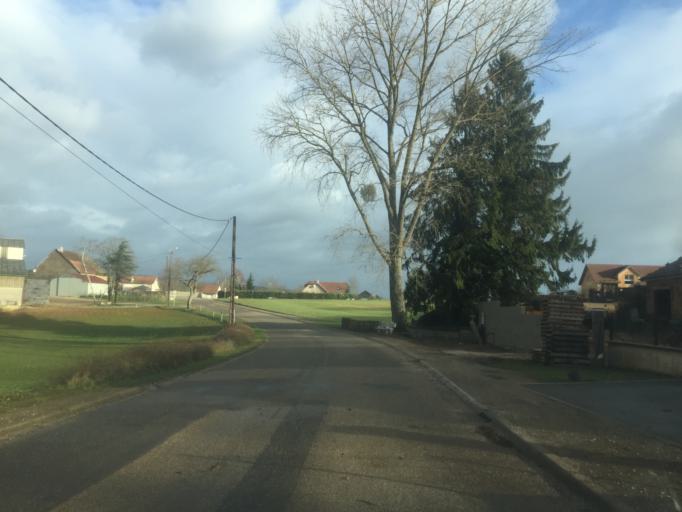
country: FR
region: Franche-Comte
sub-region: Departement du Jura
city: Orchamps
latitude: 47.2068
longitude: 5.6828
